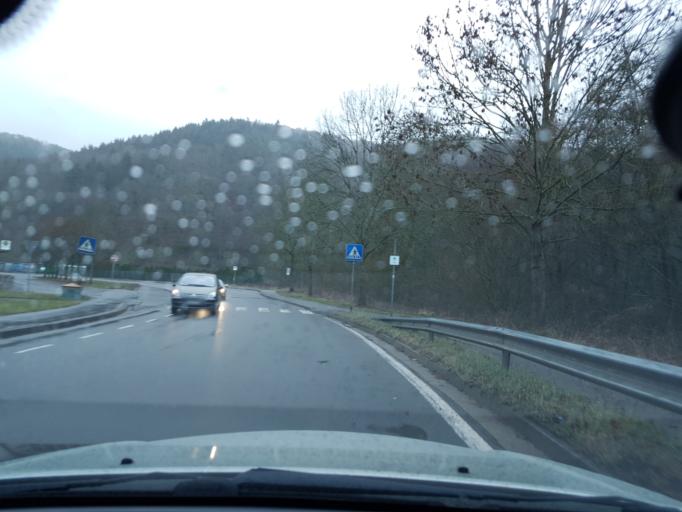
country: DE
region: Rheinland-Pfalz
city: Hintertiefenbach
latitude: 49.6997
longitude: 7.3485
